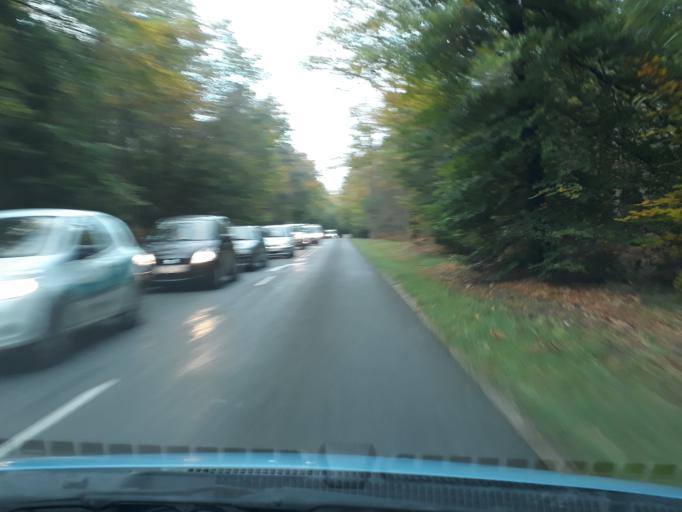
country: FR
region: Ile-de-France
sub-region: Departement de Seine-et-Marne
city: Avon
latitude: 48.3862
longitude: 2.7512
